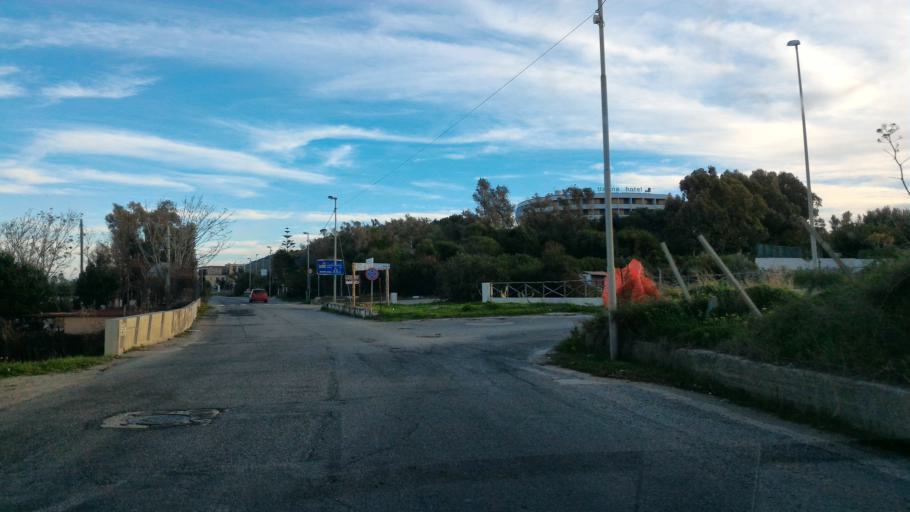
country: IT
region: Calabria
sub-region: Provincia di Crotone
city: Crotone
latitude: 39.0514
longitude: 17.1404
